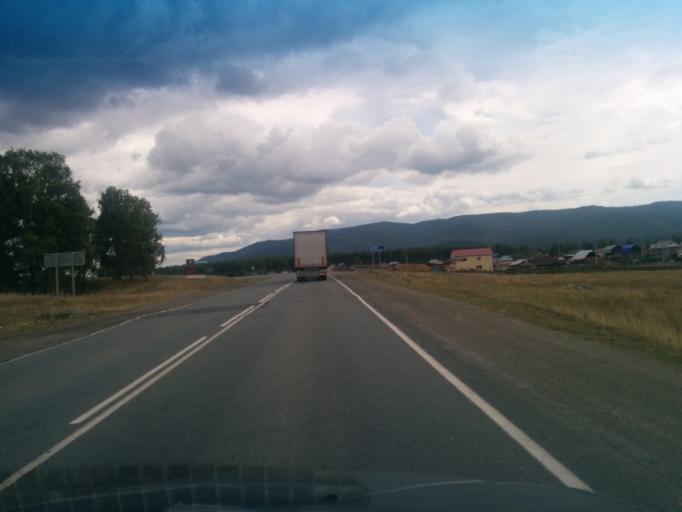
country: RU
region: Bashkortostan
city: Lomovka
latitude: 53.8847
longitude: 58.0994
